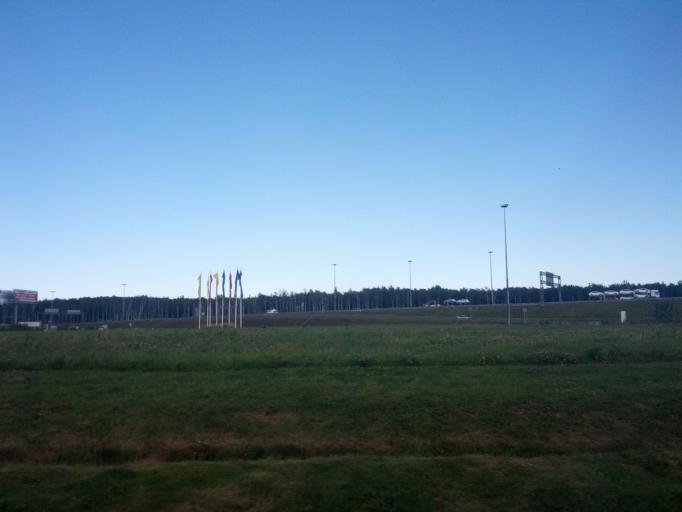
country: RU
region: Leningrad
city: Rybatskoye
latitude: 59.8952
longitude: 30.5200
